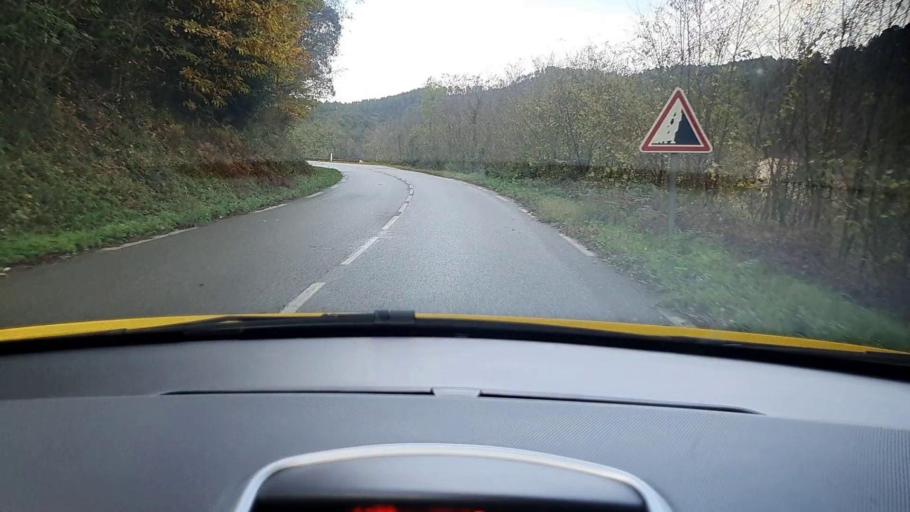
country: FR
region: Languedoc-Roussillon
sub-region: Departement du Gard
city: Lasalle
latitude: 44.1124
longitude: 3.7795
